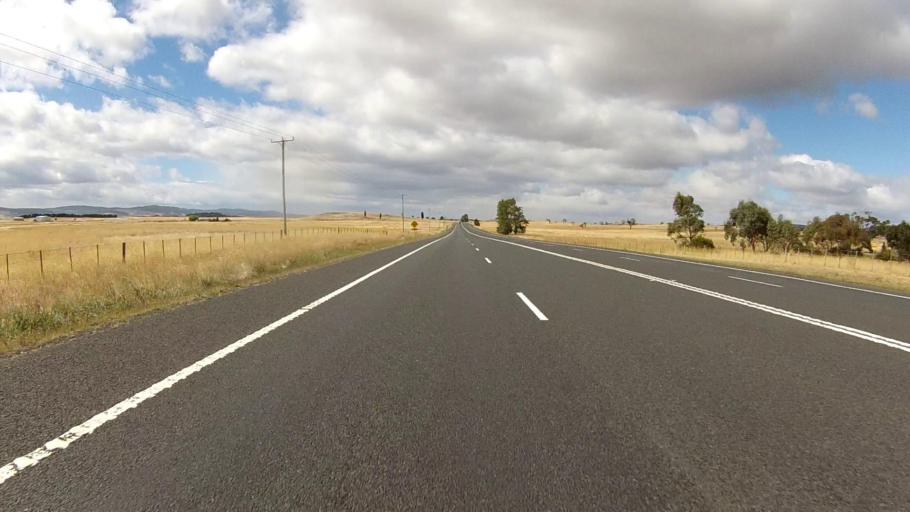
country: AU
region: Tasmania
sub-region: Northern Midlands
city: Evandale
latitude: -41.8711
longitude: 147.4604
